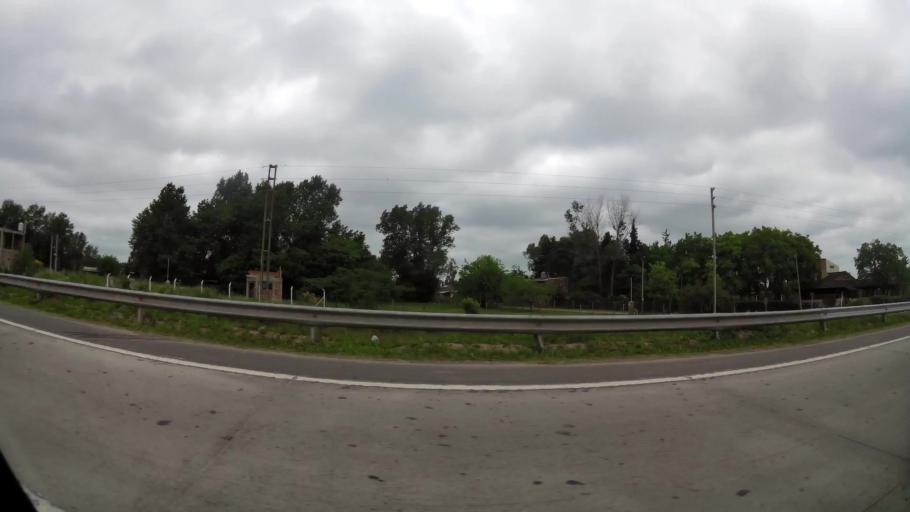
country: AR
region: Buenos Aires
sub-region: Partido de San Vicente
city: San Vicente
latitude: -35.0443
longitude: -58.4114
